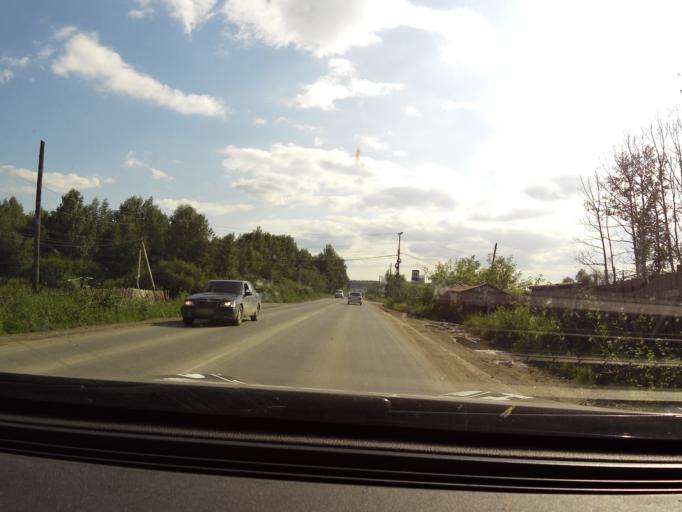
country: RU
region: Sverdlovsk
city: Shirokaya Rechka
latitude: 56.7953
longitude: 60.4895
